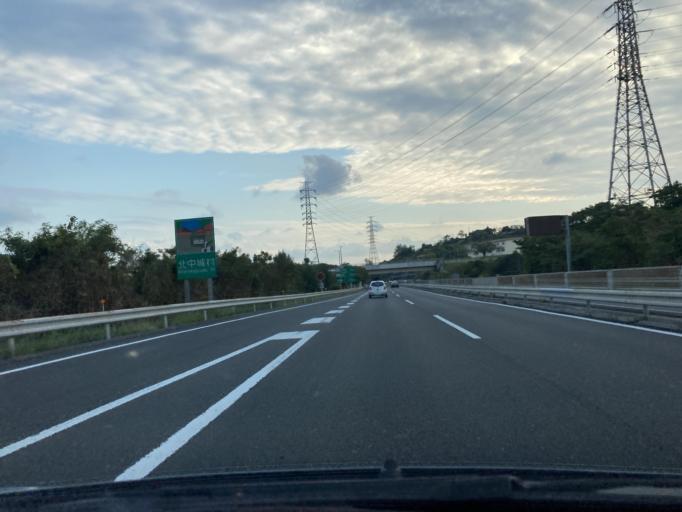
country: JP
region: Okinawa
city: Chatan
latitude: 26.3169
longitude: 127.7892
